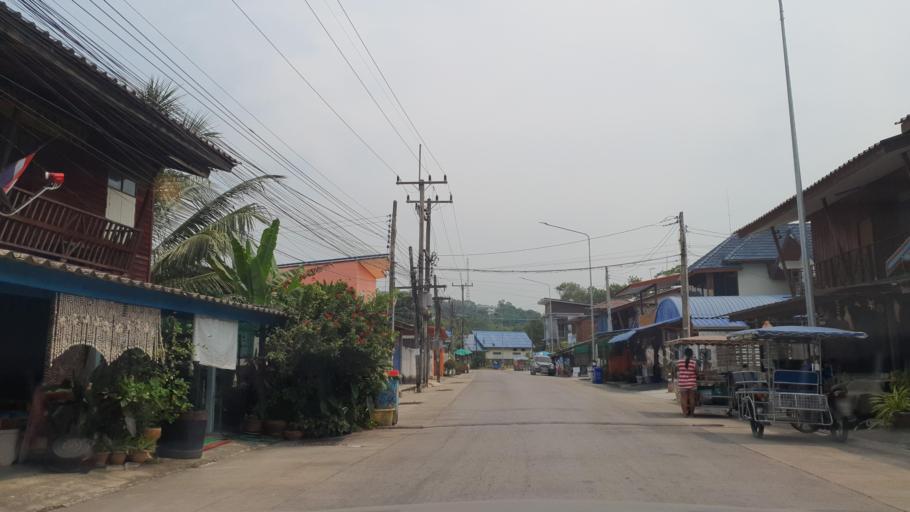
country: TH
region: Rayong
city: Rayong
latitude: 12.6126
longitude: 101.4222
